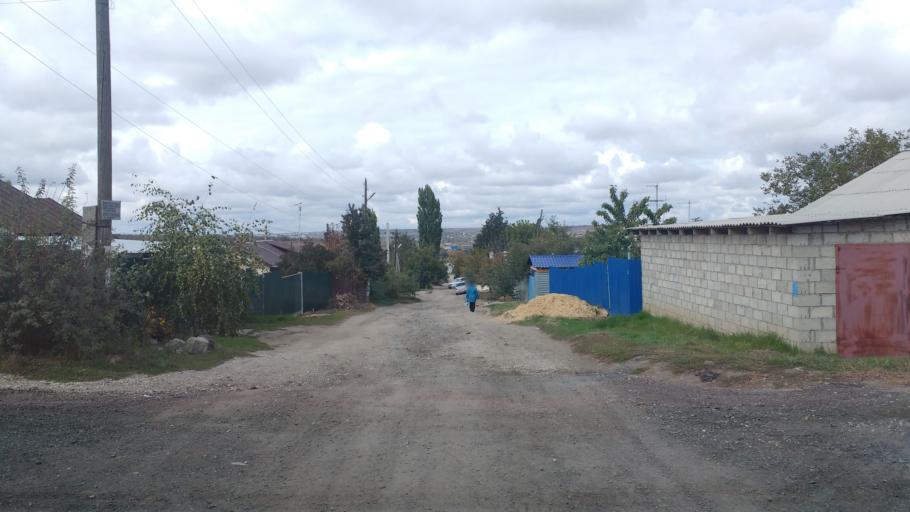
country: RU
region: Volgograd
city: Vodstroy
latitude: 48.7784
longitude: 44.5413
